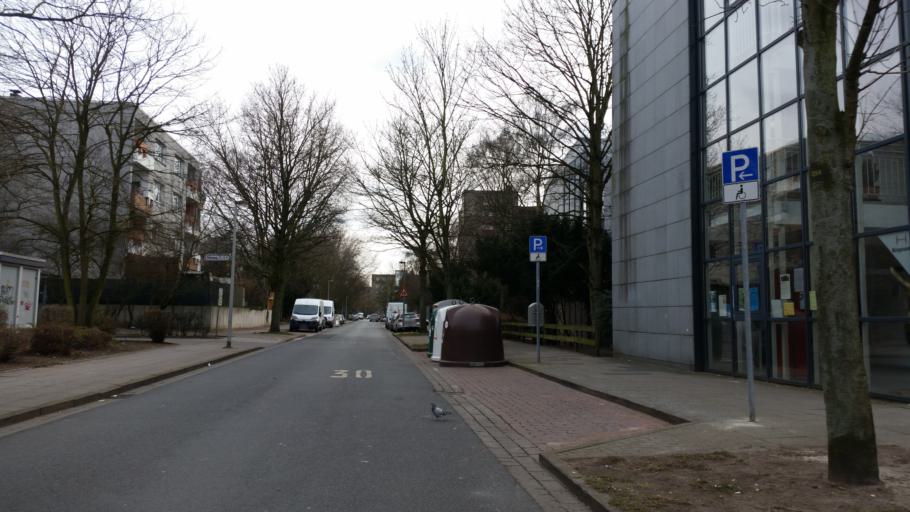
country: DE
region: Lower Saxony
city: Langenhagen
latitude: 52.4142
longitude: 9.7793
